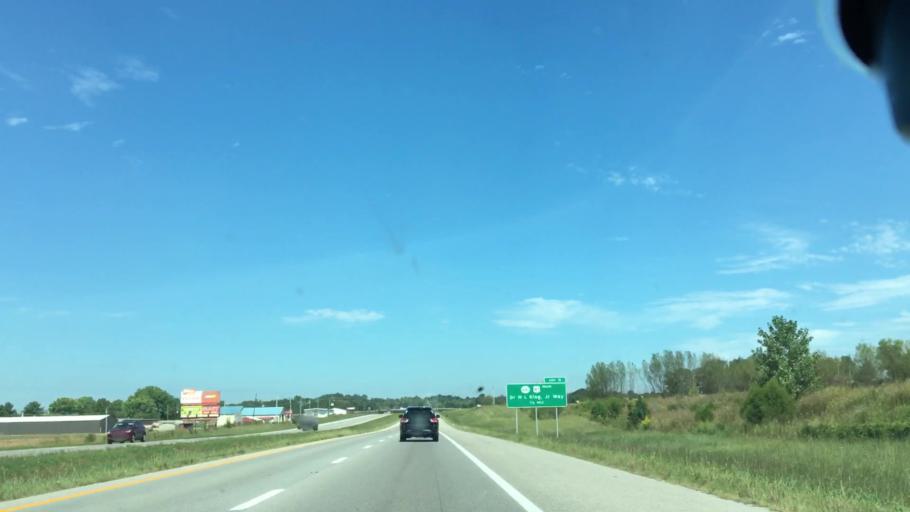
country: US
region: Kentucky
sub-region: Christian County
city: Hopkinsville
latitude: 36.8866
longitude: -87.4687
